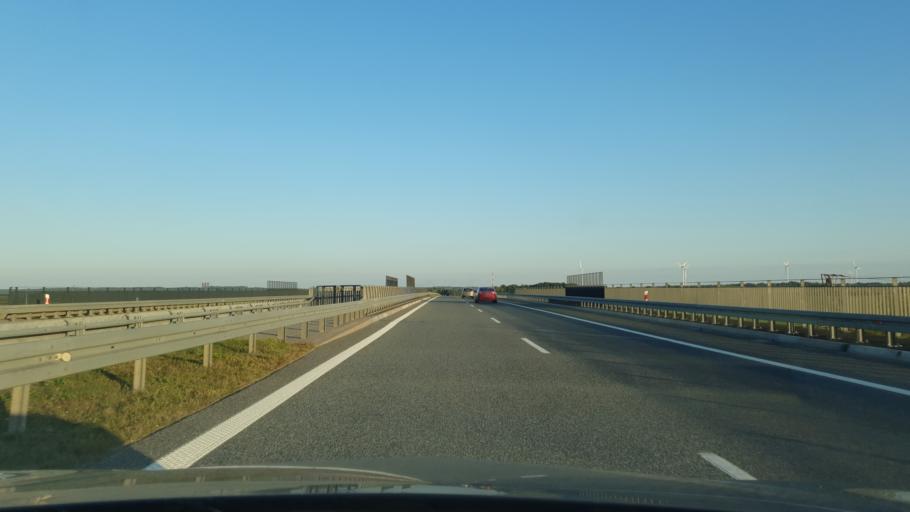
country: PL
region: Pomeranian Voivodeship
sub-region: Powiat slupski
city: Kobylnica
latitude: 54.4383
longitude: 16.9536
